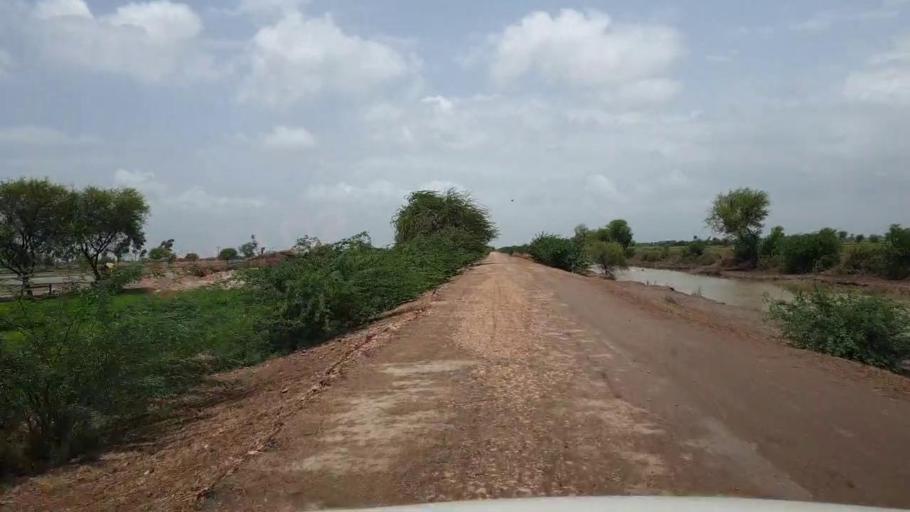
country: PK
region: Sindh
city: Kario
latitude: 24.7099
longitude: 68.6004
